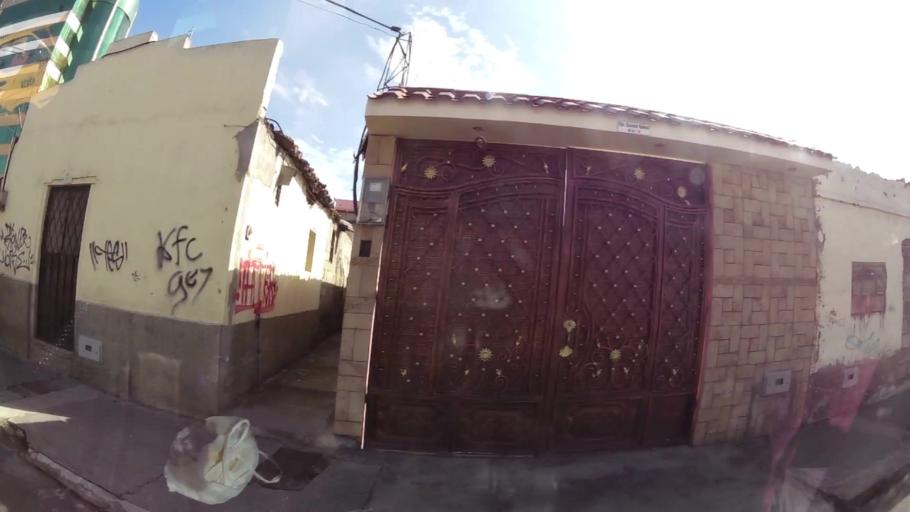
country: EC
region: Chimborazo
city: Riobamba
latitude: -1.6634
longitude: -78.6596
